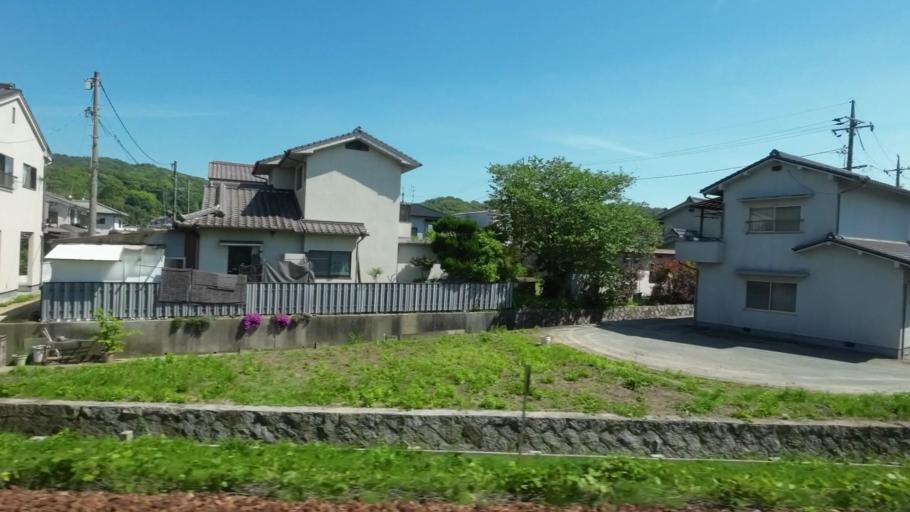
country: JP
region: Hiroshima
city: Onomichi
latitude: 34.4537
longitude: 133.2654
